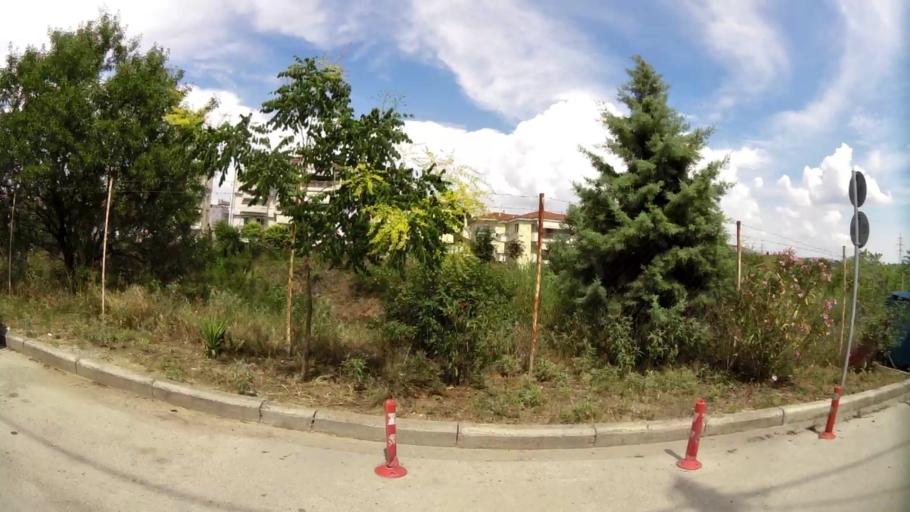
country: GR
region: Central Macedonia
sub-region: Nomos Thessalonikis
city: Pylaia
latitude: 40.5958
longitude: 22.9792
